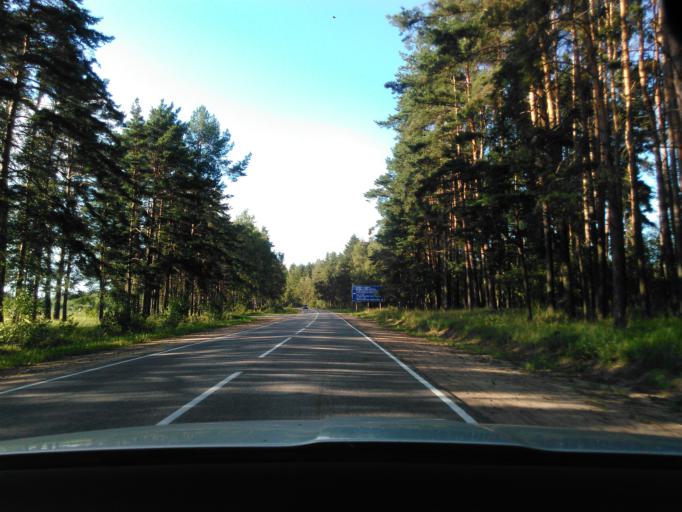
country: RU
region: Tverskaya
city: Zavidovo
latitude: 56.5903
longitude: 36.5414
